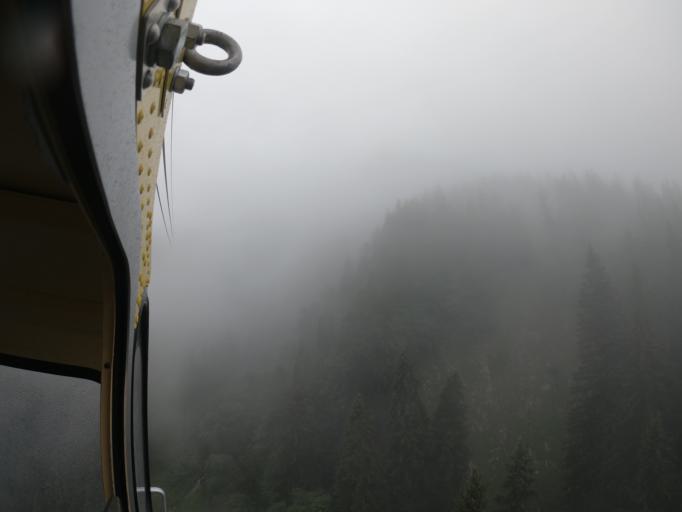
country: DE
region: Bavaria
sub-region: Upper Bavaria
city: Aschau im Chiemgau
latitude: 47.7567
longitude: 12.3440
